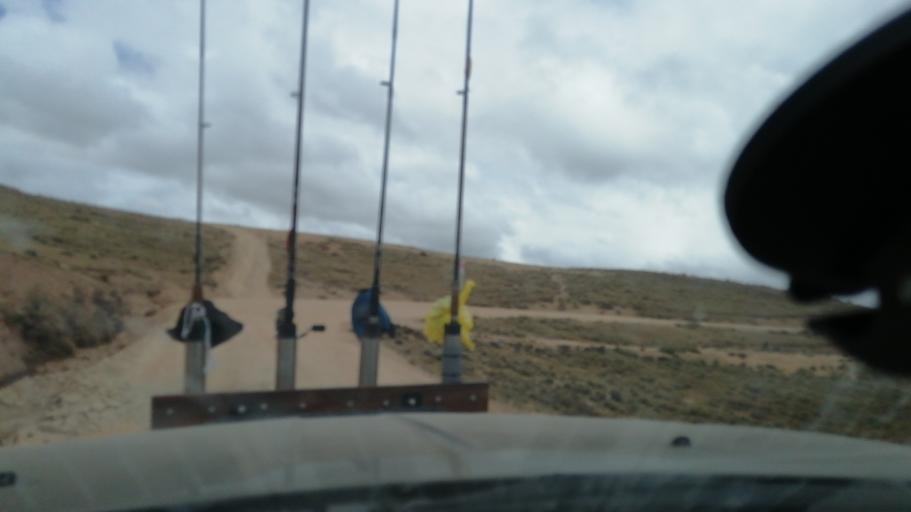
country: PE
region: Huancavelica
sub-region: Provincia de Huancavelica
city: Acobambilla
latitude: -12.5796
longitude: -75.5355
